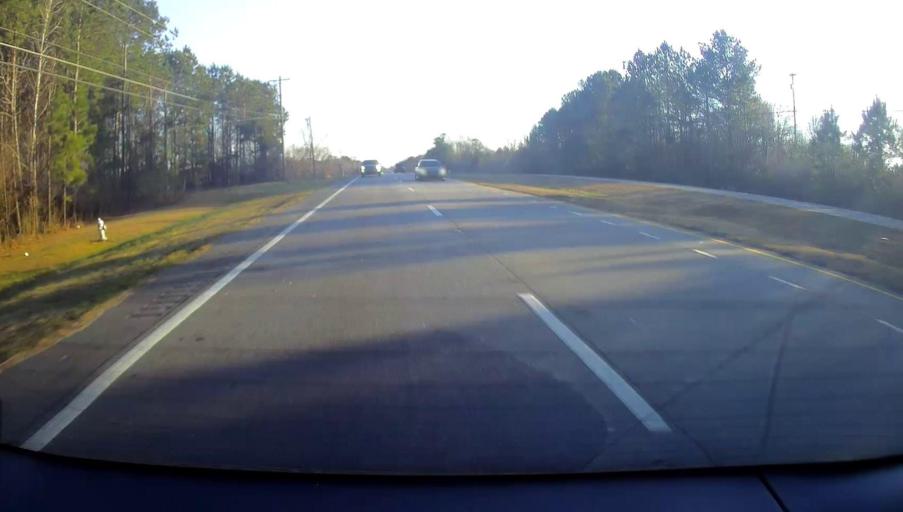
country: US
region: Georgia
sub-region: Fulton County
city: Fairburn
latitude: 33.5204
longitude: -84.5761
